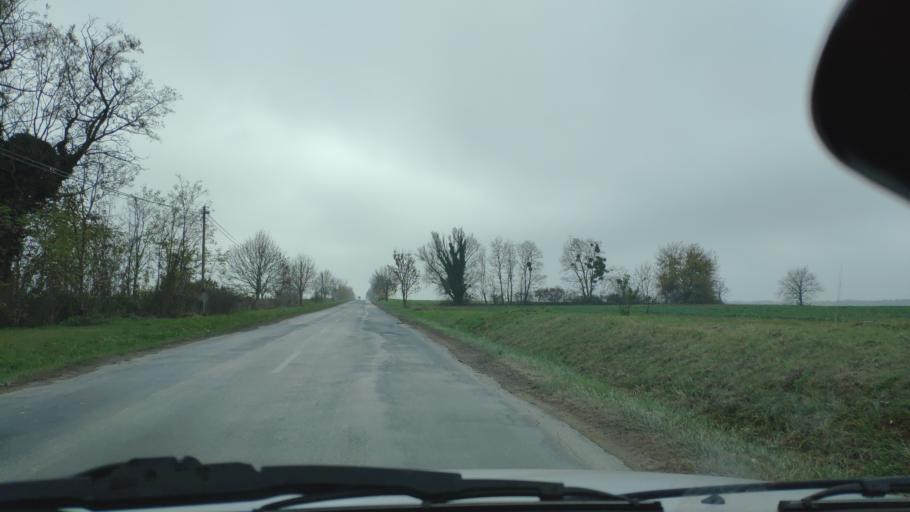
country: HU
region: Somogy
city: Balatonbereny
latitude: 46.6681
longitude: 17.2919
